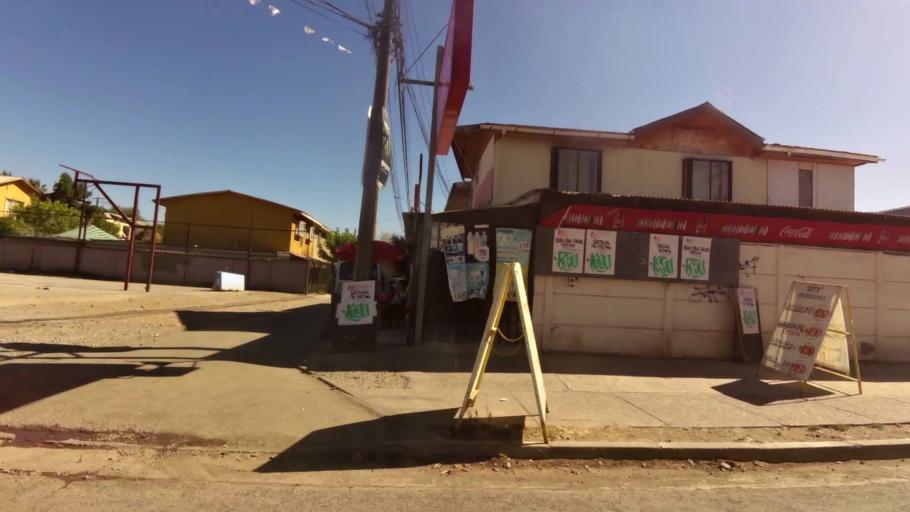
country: CL
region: O'Higgins
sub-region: Provincia de Colchagua
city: Chimbarongo
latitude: -34.5765
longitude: -71.0047
